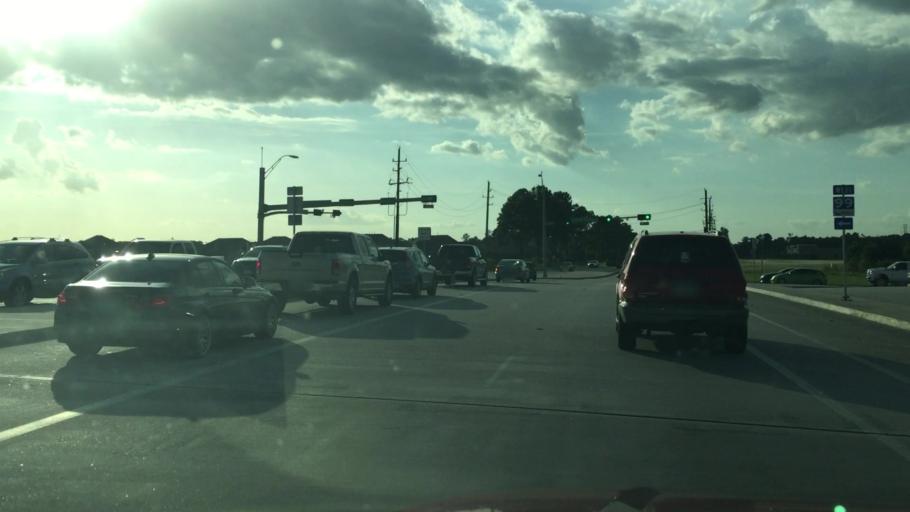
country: US
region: Texas
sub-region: Harris County
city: Tomball
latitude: 30.0753
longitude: -95.5566
